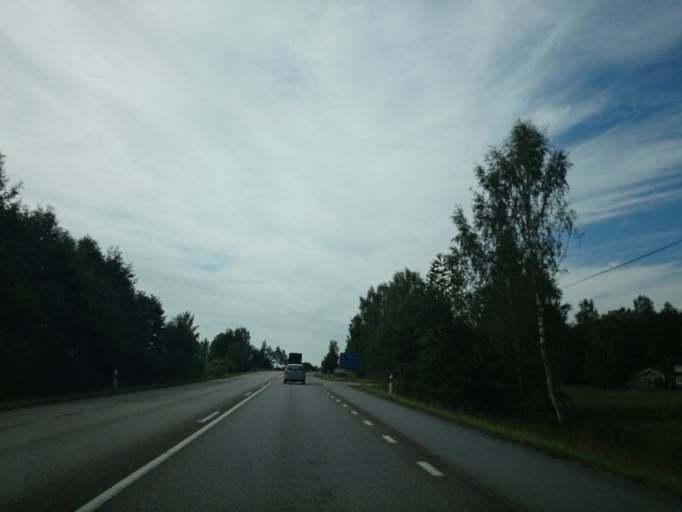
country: SE
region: Kalmar
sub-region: Vasterviks Kommun
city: Ankarsrum
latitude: 57.7165
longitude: 16.4502
